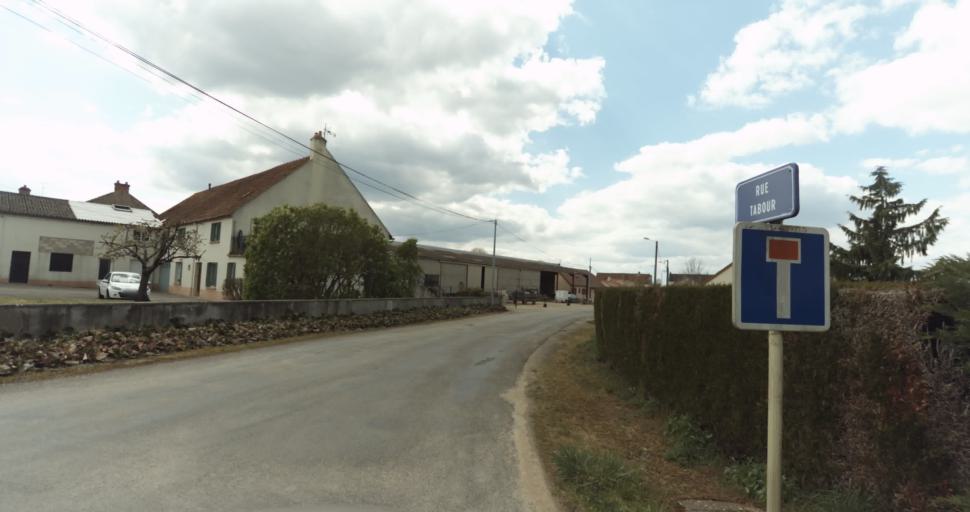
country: FR
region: Bourgogne
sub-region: Departement de la Cote-d'Or
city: Auxonne
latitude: 47.1842
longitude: 5.3914
